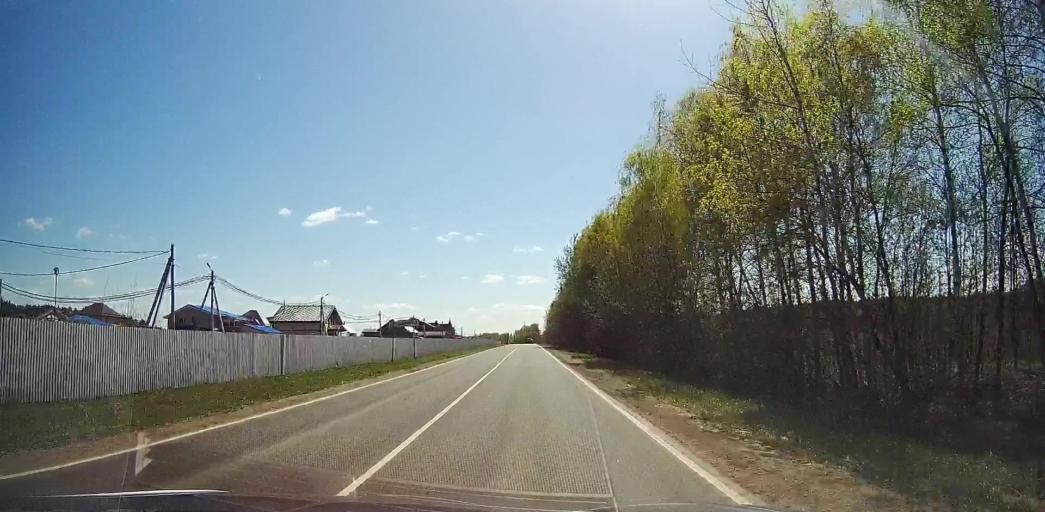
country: RU
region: Moskovskaya
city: Beloozerskiy
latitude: 55.5339
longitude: 38.4281
